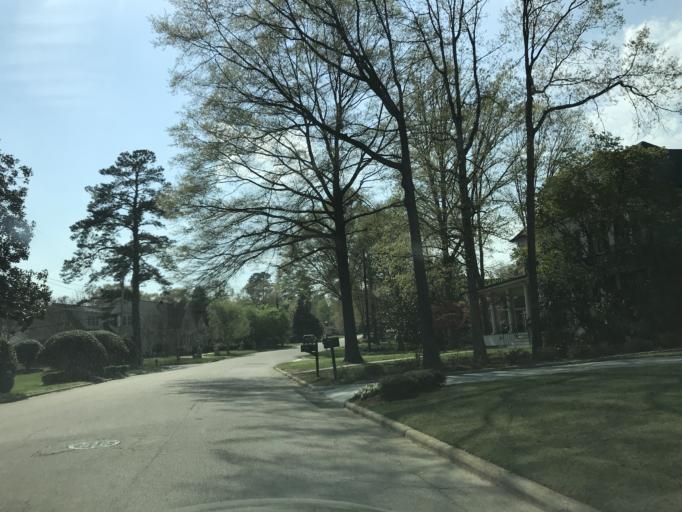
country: US
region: North Carolina
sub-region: Wake County
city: West Raleigh
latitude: 35.8058
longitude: -78.6813
